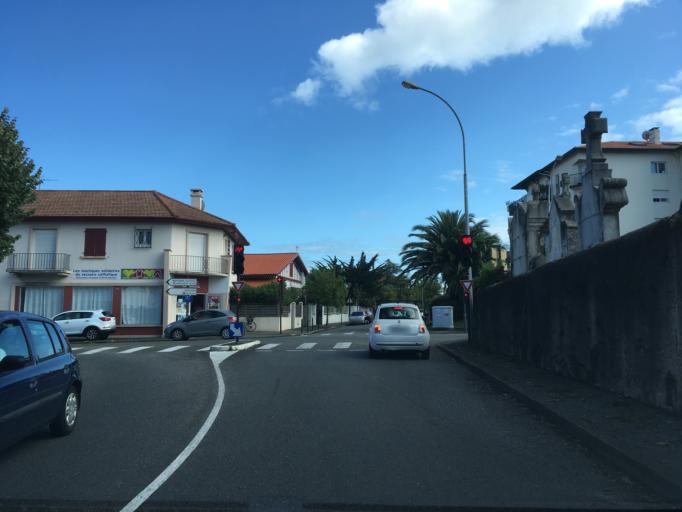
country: FR
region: Aquitaine
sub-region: Departement des Pyrenees-Atlantiques
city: Biarritz
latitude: 43.4740
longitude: -1.5551
